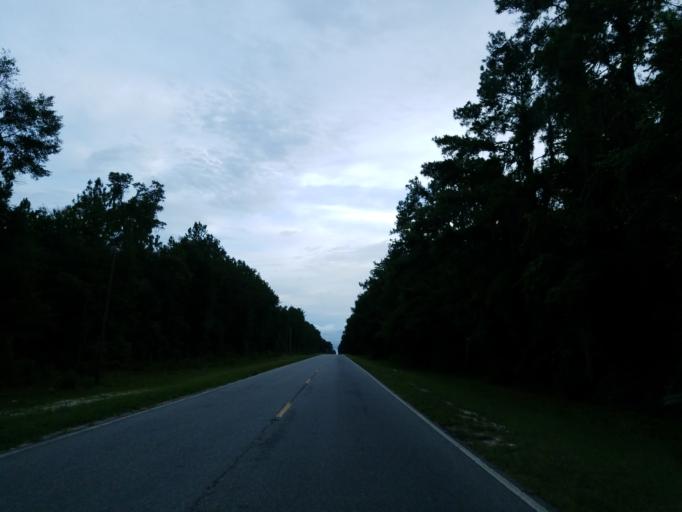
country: US
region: Georgia
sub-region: Echols County
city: Statenville
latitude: 30.6935
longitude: -83.0276
